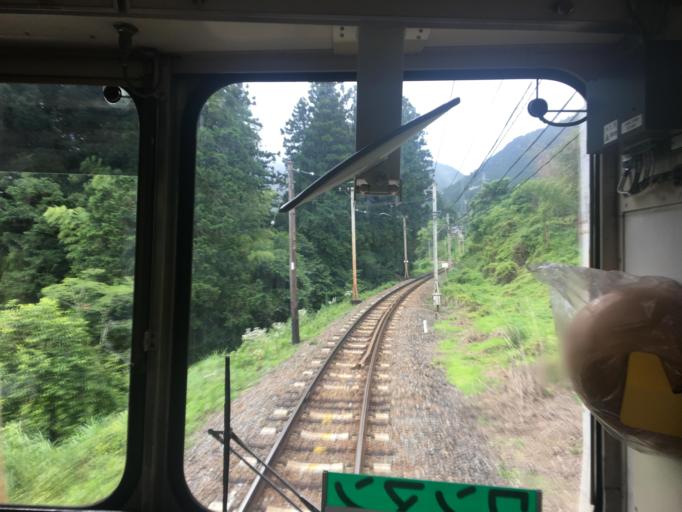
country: JP
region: Saitama
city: Chichibu
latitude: 35.9655
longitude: 139.0503
